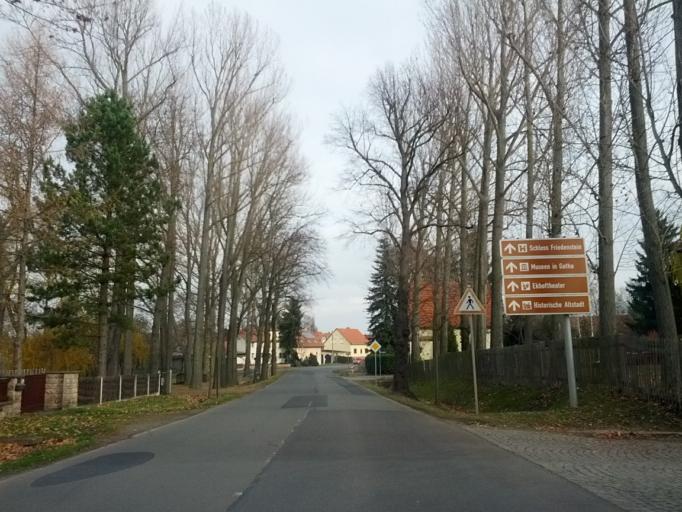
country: DE
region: Thuringia
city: Gotha
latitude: 50.9261
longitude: 10.6643
